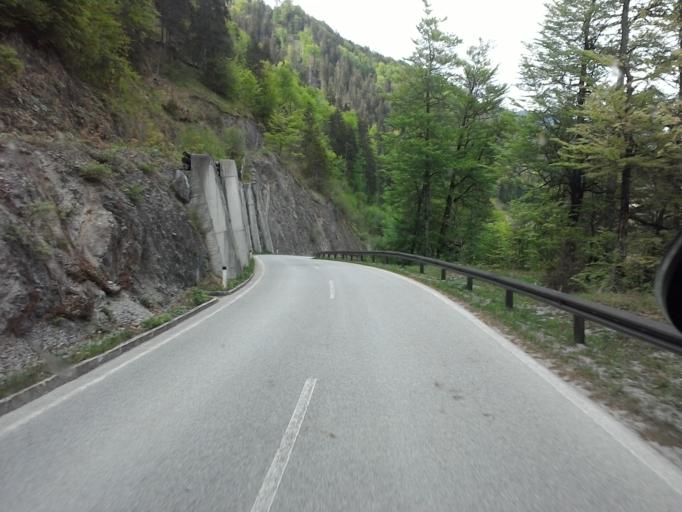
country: AT
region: Styria
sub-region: Politischer Bezirk Liezen
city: Gams bei Hieflau
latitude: 47.6797
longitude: 14.7668
